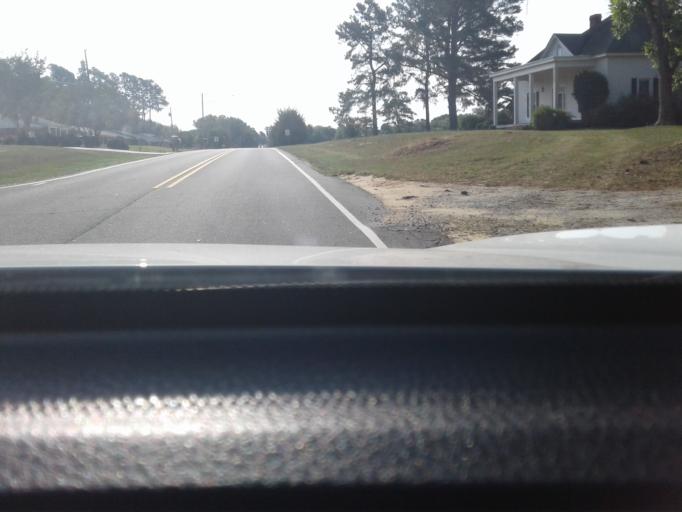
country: US
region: North Carolina
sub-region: Johnston County
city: Benson
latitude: 35.3881
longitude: -78.5674
